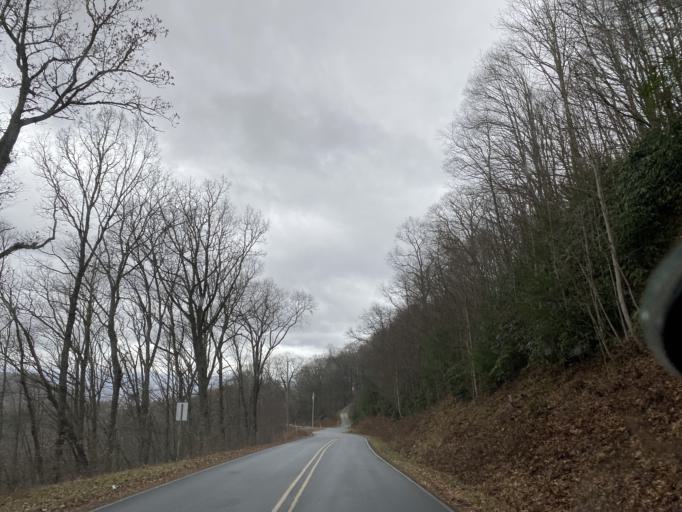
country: US
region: North Carolina
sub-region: Jackson County
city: Cullowhee
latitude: 35.2163
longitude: -83.1812
